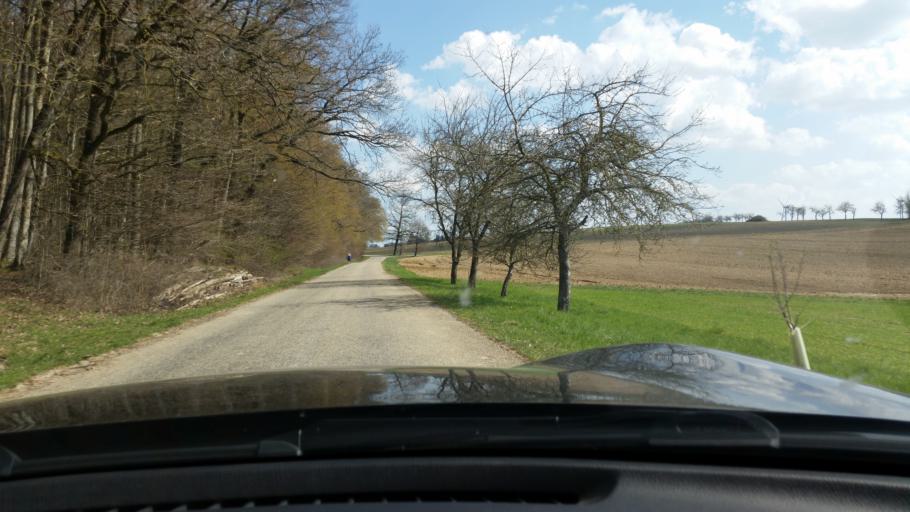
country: DE
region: Baden-Wuerttemberg
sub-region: Regierungsbezirk Stuttgart
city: Langenburg
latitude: 49.2949
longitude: 9.8490
